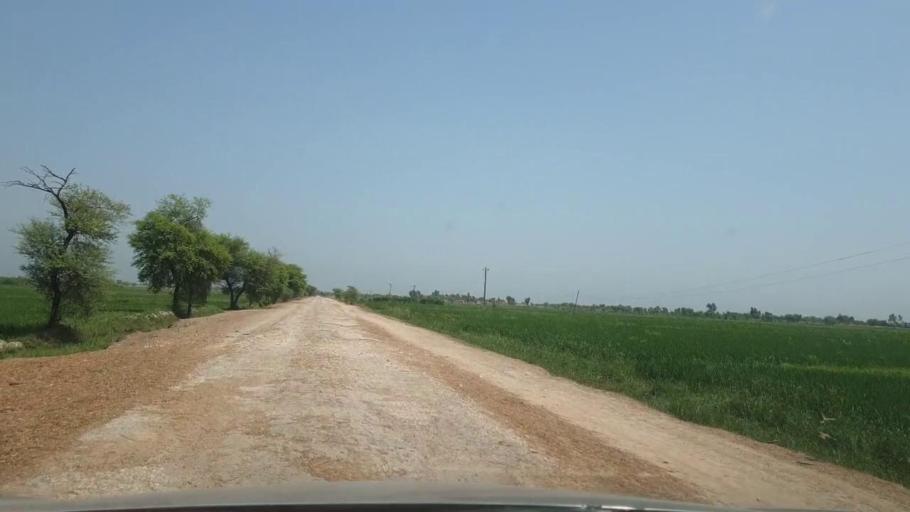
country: PK
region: Sindh
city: Warah
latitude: 27.5092
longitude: 67.7810
